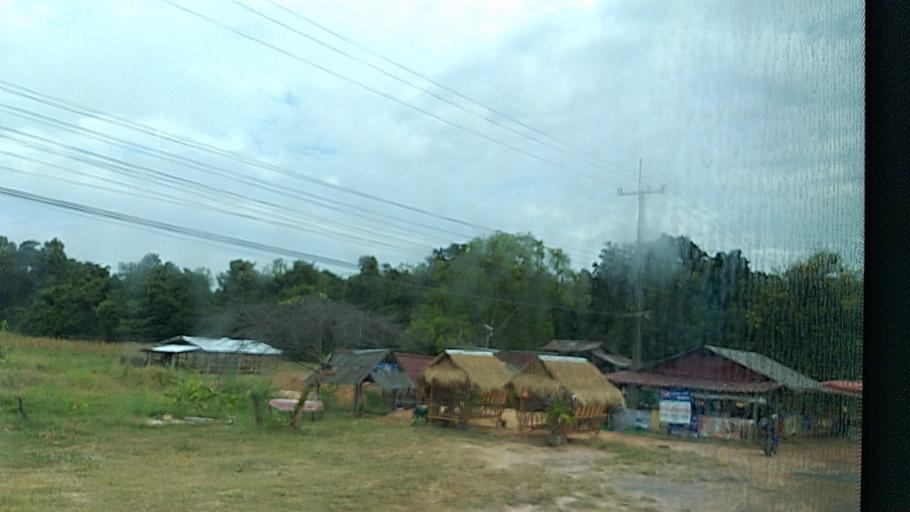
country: TH
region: Kalasin
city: Khong Chai
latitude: 16.1339
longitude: 103.4533
